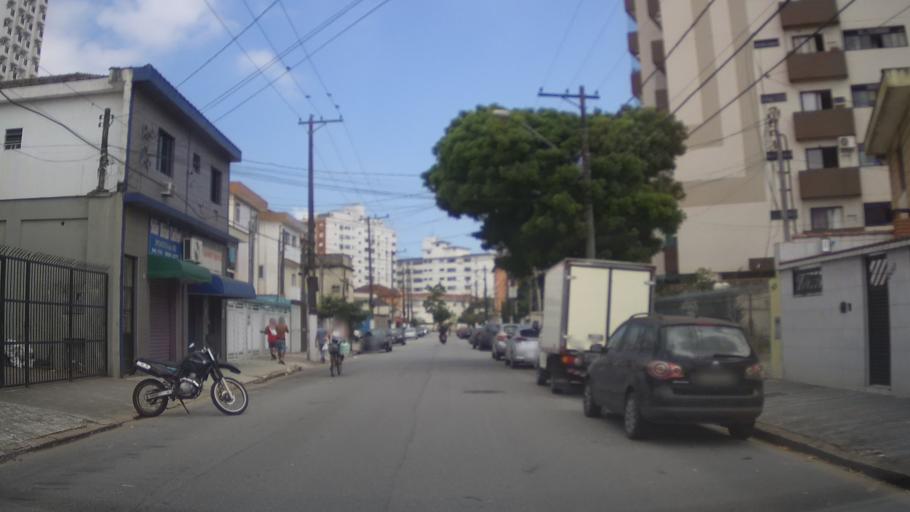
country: BR
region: Sao Paulo
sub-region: Santos
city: Santos
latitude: -23.9622
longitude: -46.3126
